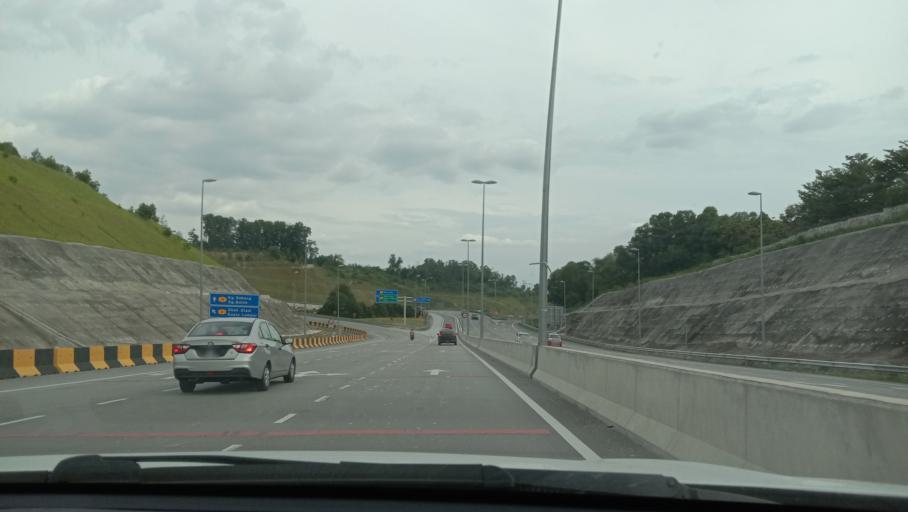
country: MY
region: Selangor
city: Kampung Baru Subang
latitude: 3.1266
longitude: 101.5235
